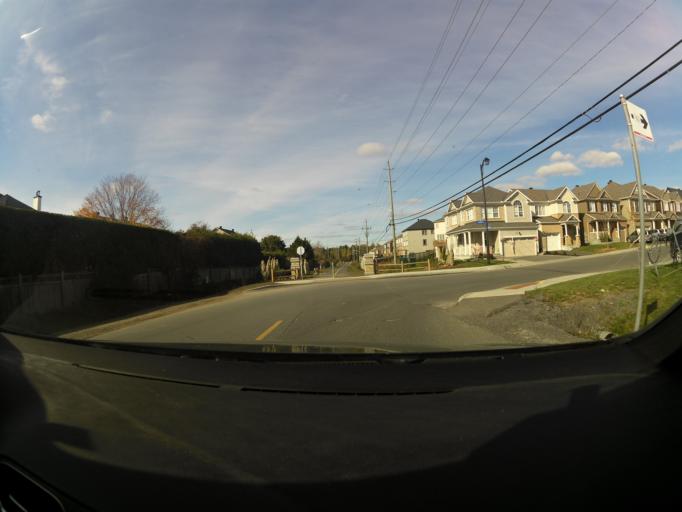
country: CA
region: Ontario
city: Bells Corners
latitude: 45.2808
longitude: -75.9261
